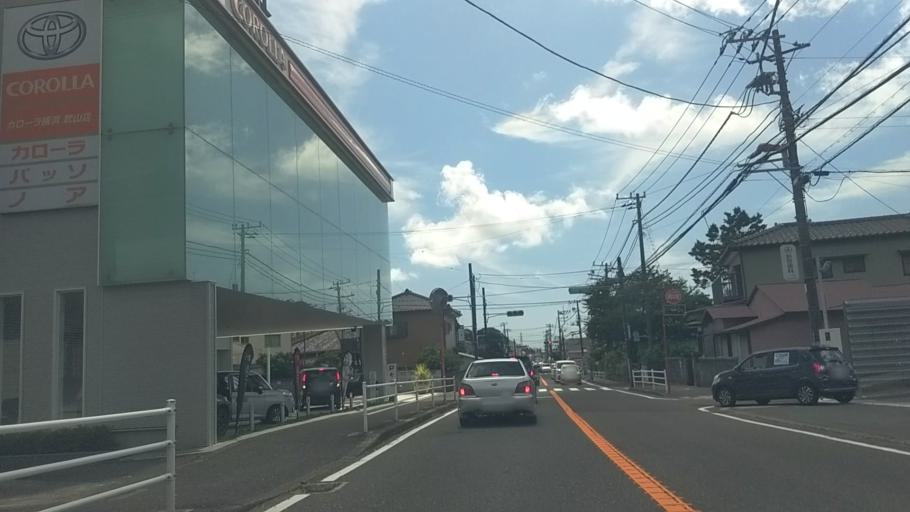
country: JP
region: Kanagawa
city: Yokosuka
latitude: 35.2234
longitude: 139.6441
